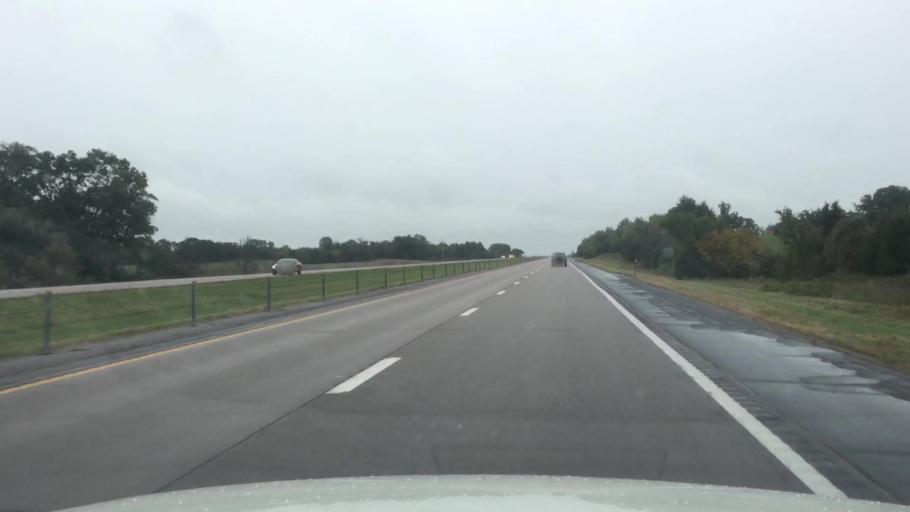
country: US
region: Missouri
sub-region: Boone County
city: Ashland
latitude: 38.7243
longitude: -92.2544
